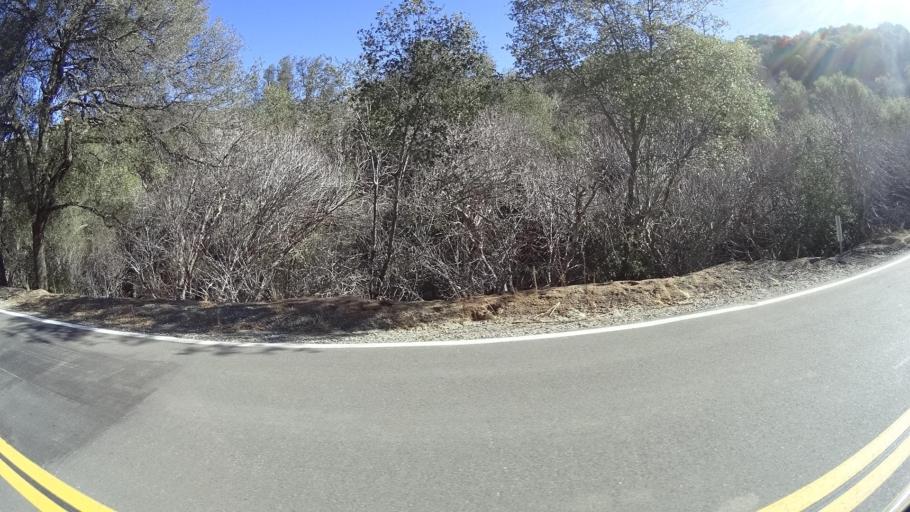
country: US
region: California
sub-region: Kern County
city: Alta Sierra
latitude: 35.7373
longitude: -118.6534
